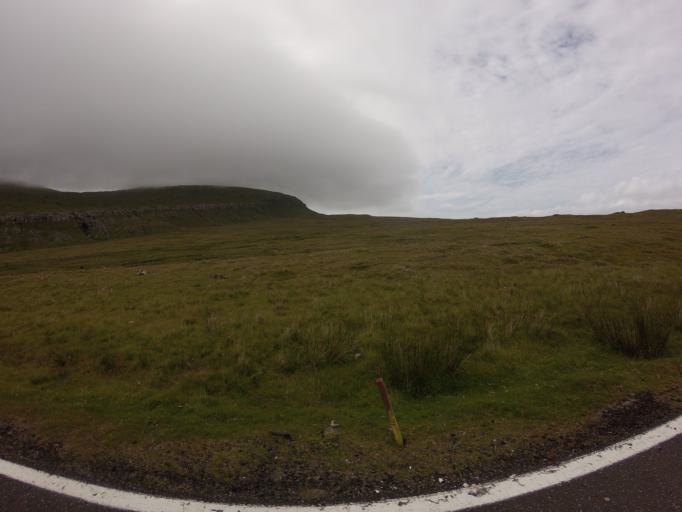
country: FO
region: Sandoy
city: Sandur
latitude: 61.8193
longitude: -6.7197
